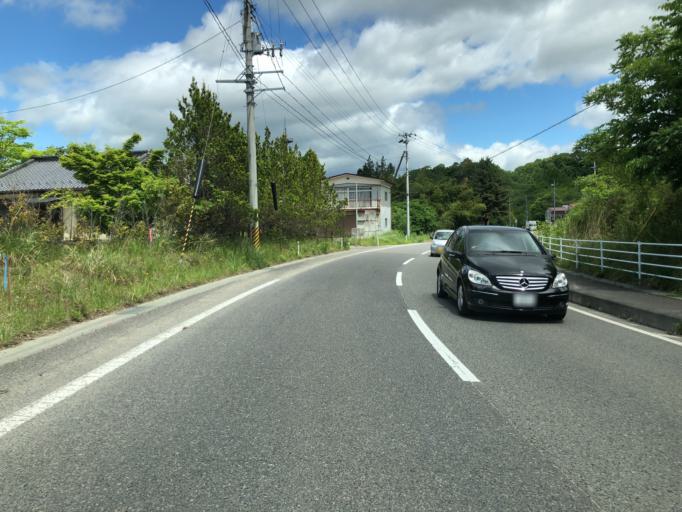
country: JP
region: Fukushima
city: Motomiya
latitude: 37.5043
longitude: 140.4123
